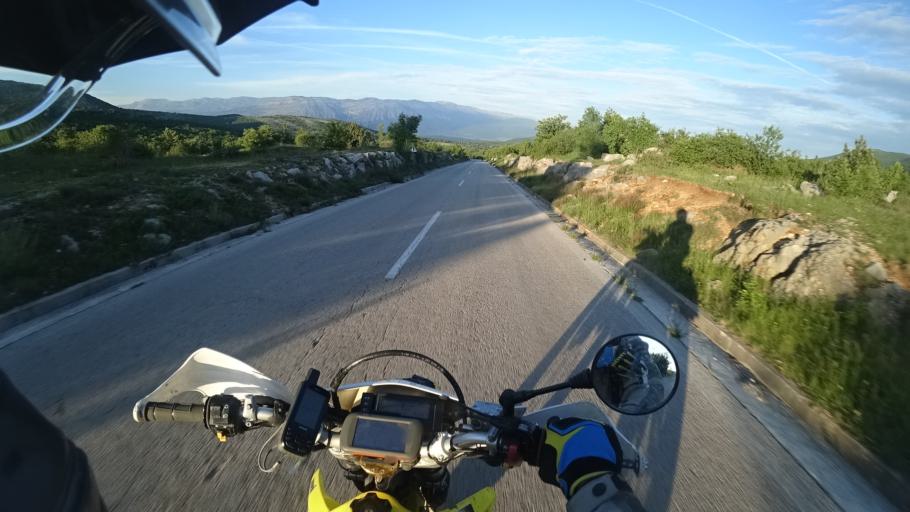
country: HR
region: Sibensko-Kniniska
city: Drnis
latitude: 43.8926
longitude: 16.3553
